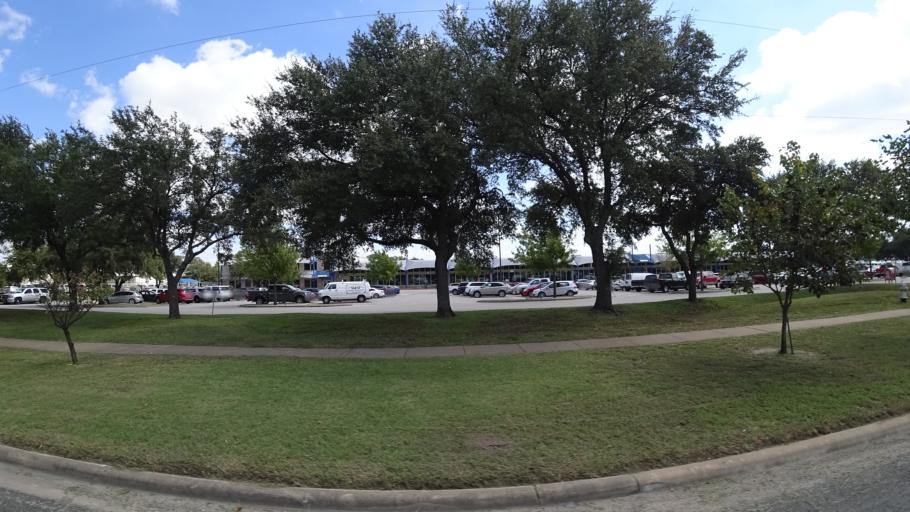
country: US
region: Texas
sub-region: Travis County
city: Austin
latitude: 30.3168
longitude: -97.7137
